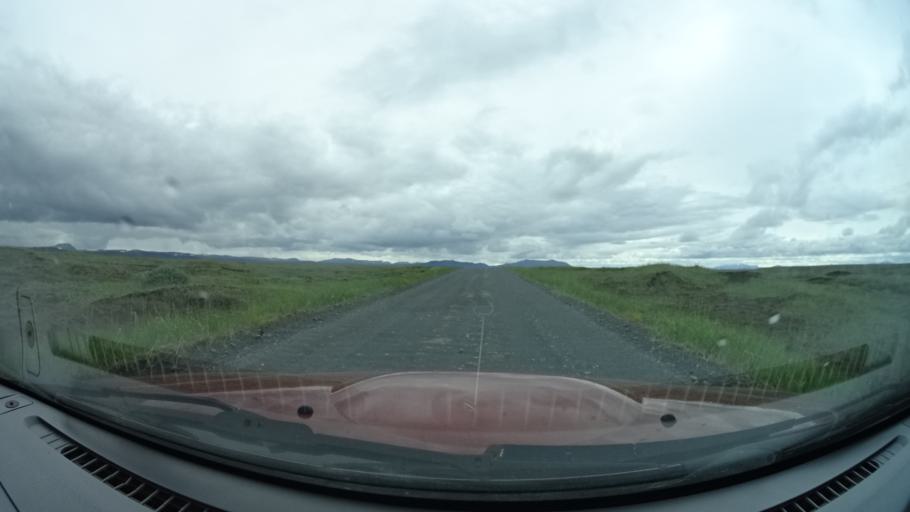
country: IS
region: Northeast
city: Laugar
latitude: 65.6660
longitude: -16.1605
